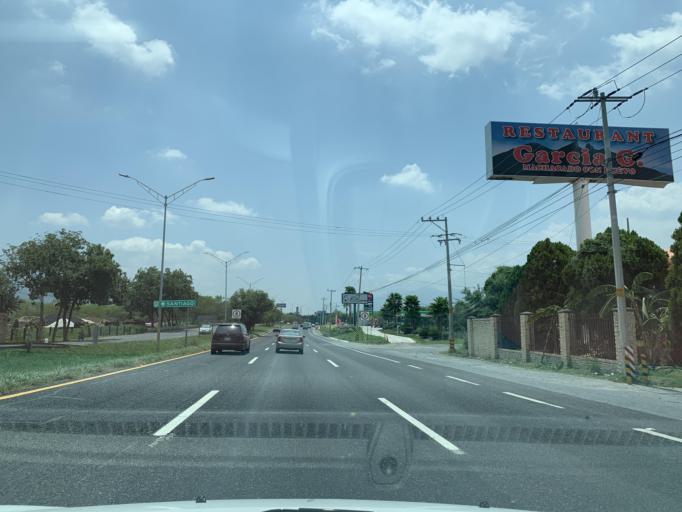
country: MX
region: Nuevo Leon
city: Santiago
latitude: 25.4891
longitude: -100.1843
